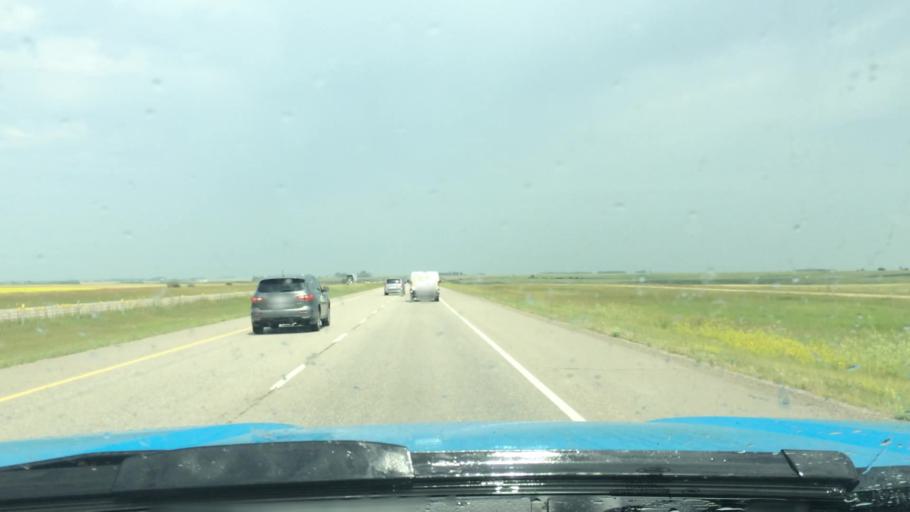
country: CA
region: Alberta
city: Carstairs
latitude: 51.6251
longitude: -114.0253
